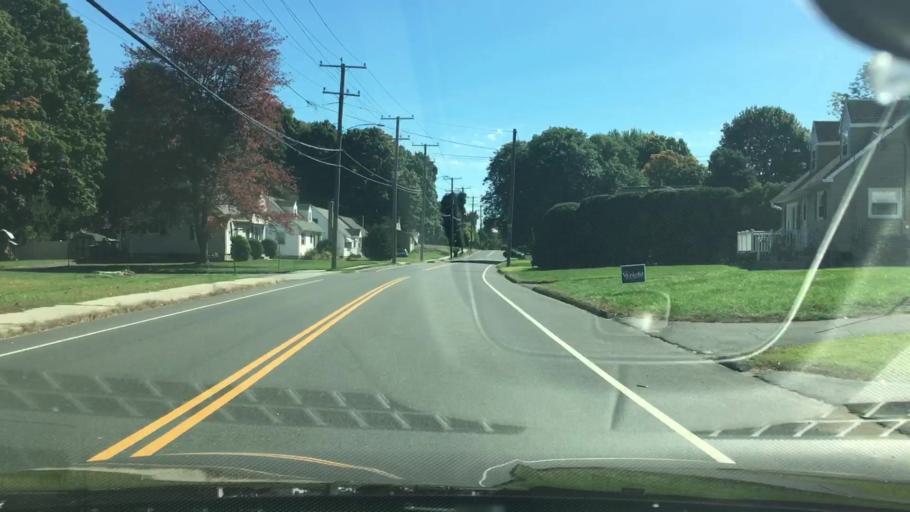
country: US
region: Connecticut
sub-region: Hartford County
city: Bristol
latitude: 41.6842
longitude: -72.9088
